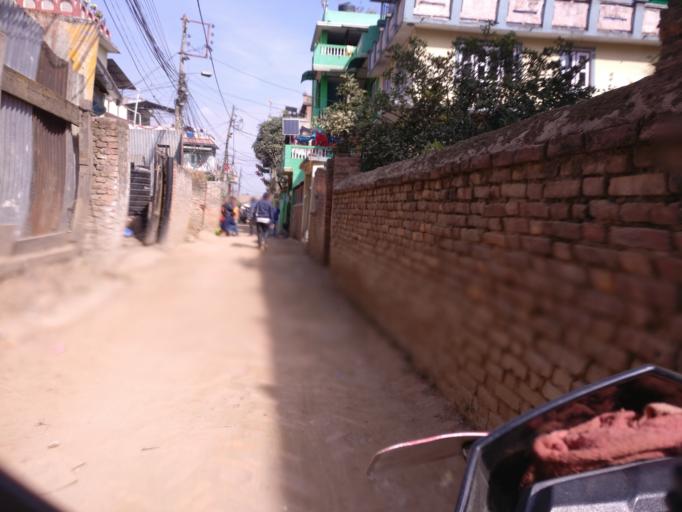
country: NP
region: Central Region
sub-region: Bagmati Zone
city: Patan
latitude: 27.6601
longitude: 85.3244
